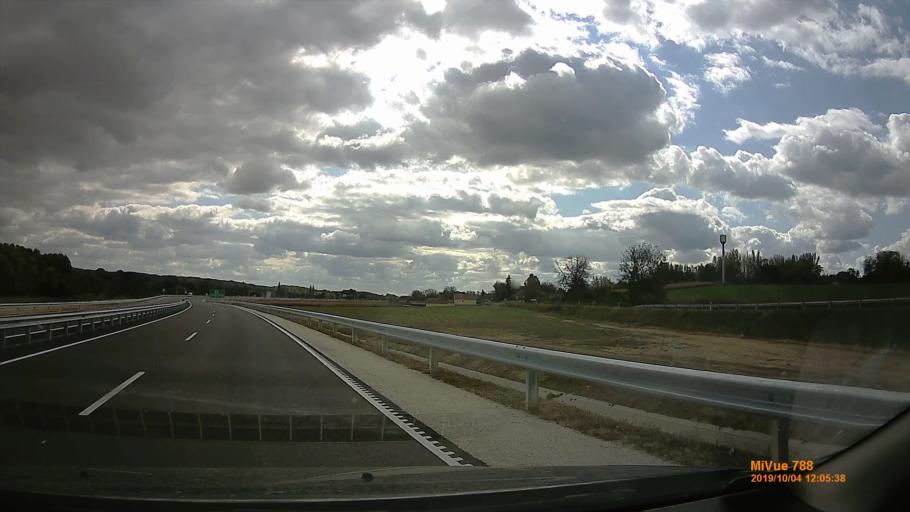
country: HU
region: Somogy
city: Karad
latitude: 46.5588
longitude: 17.8105
